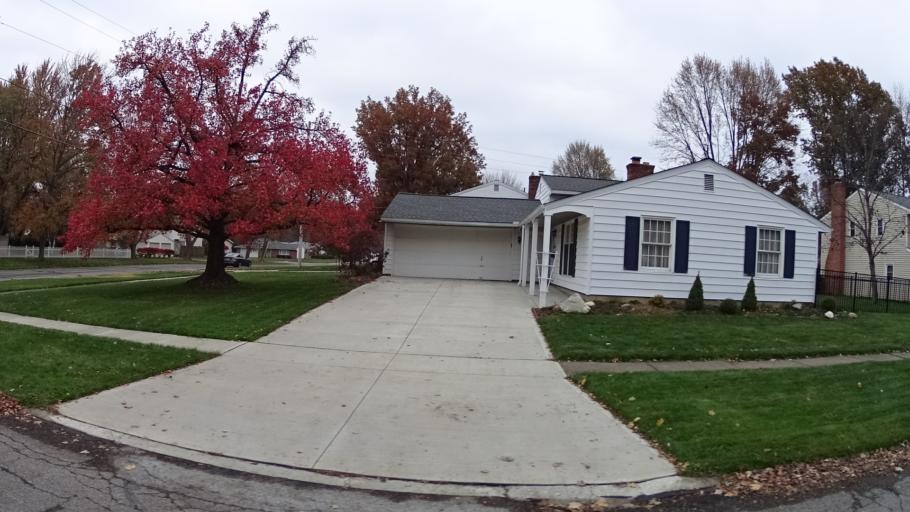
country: US
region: Ohio
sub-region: Lorain County
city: Elyria
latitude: 41.3533
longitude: -82.0945
